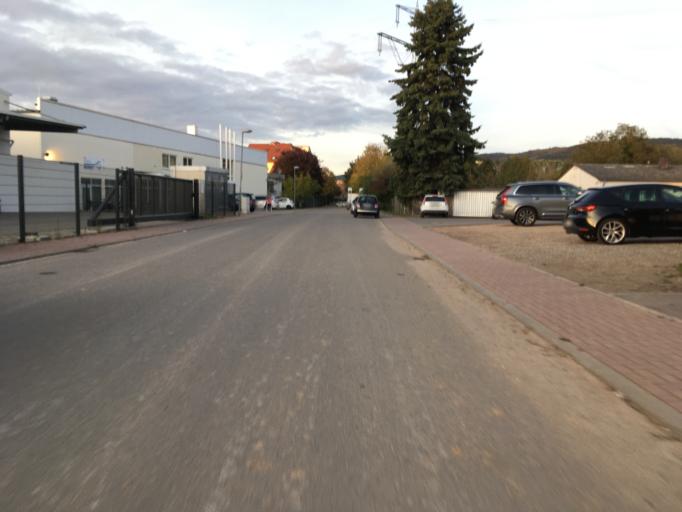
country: DE
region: Baden-Wuerttemberg
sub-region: Karlsruhe Region
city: Leimen
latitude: 49.3408
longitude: 8.6836
